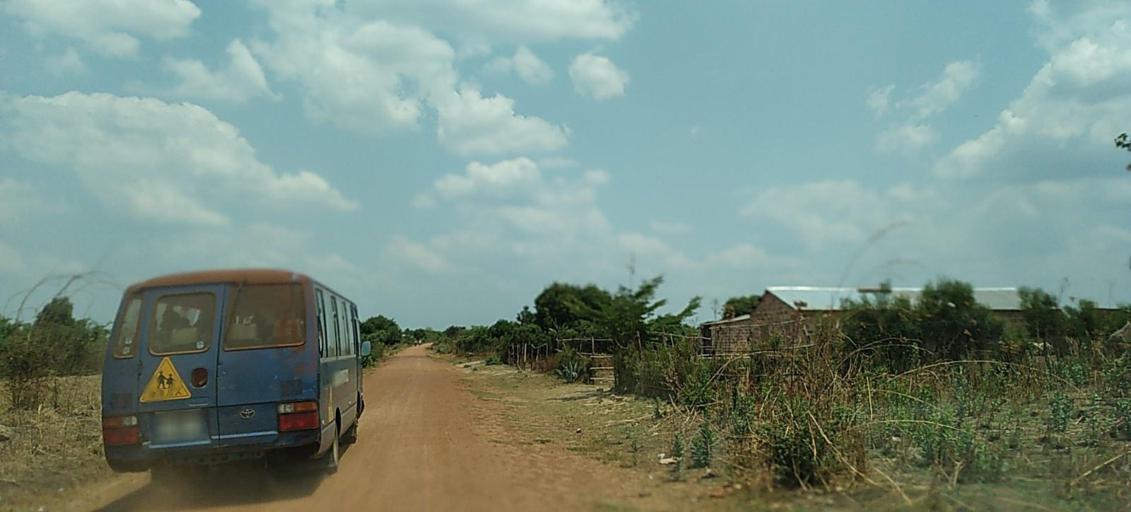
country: ZM
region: Copperbelt
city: Luanshya
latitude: -13.1285
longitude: 28.3115
